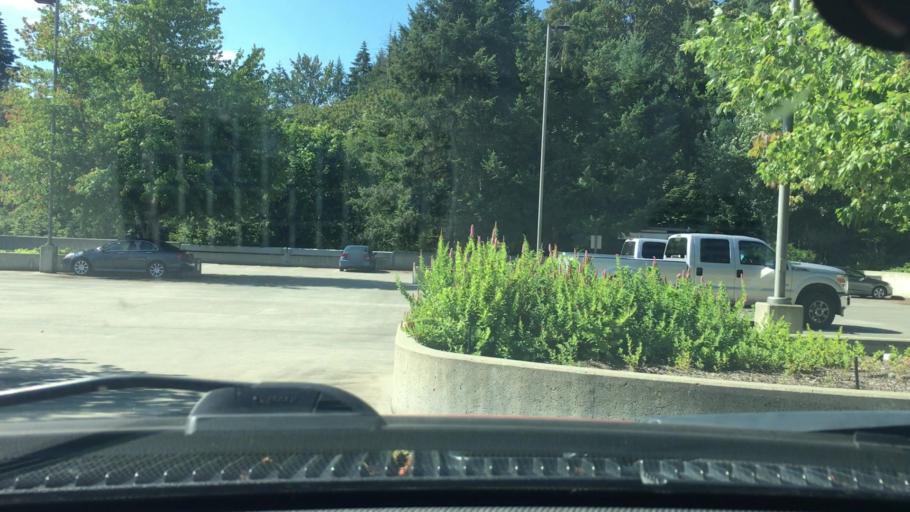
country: US
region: Washington
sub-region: King County
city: Redmond
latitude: 47.6427
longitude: -122.1227
